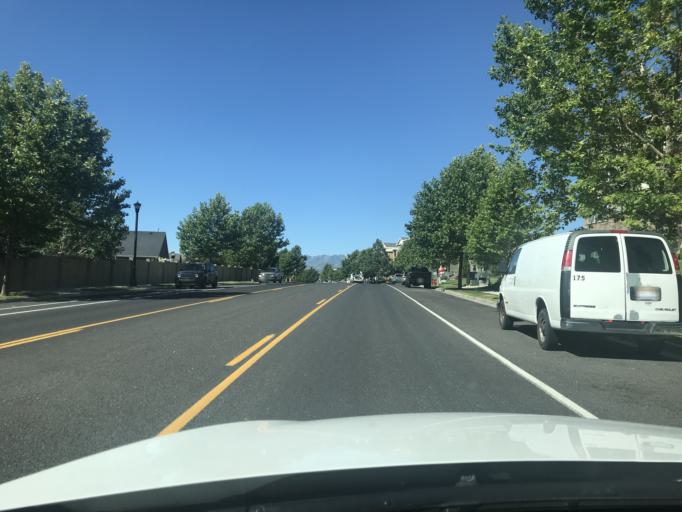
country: US
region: Utah
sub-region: Salt Lake County
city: South Jordan Heights
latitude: 40.5502
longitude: -111.9781
